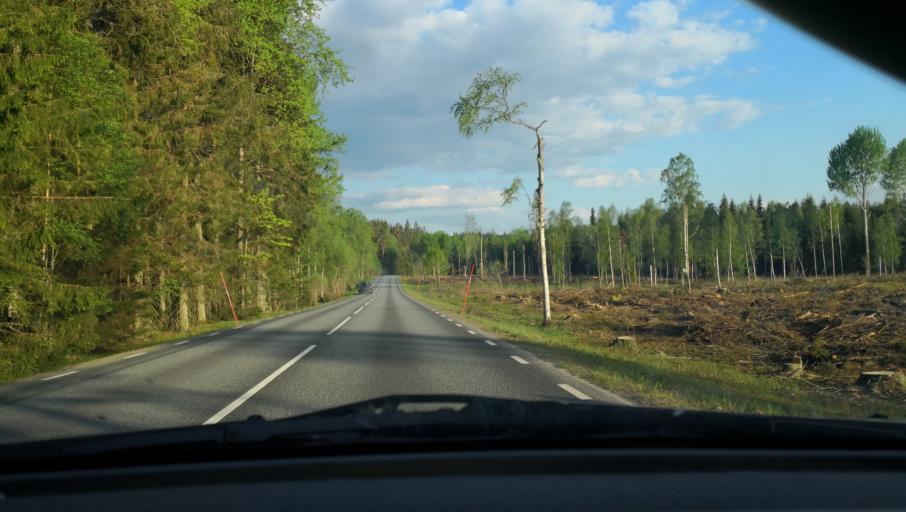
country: SE
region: Joenkoeping
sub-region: Vetlanda Kommun
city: Landsbro
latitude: 57.3874
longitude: 14.8370
